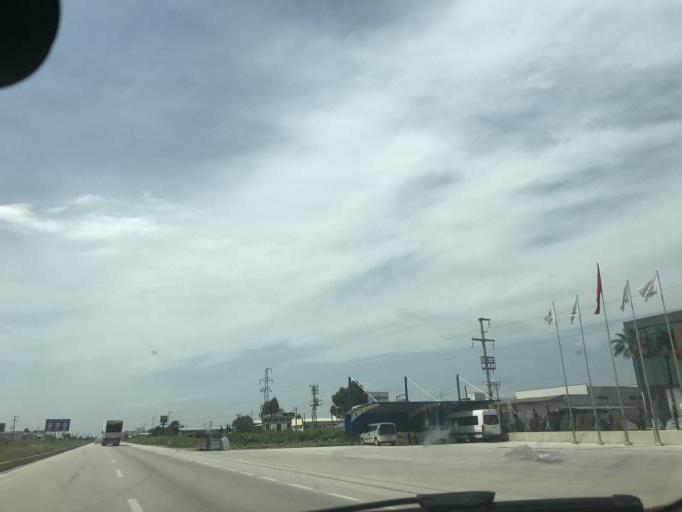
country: TR
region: Adana
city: Yuregir
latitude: 36.9782
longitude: 35.4663
